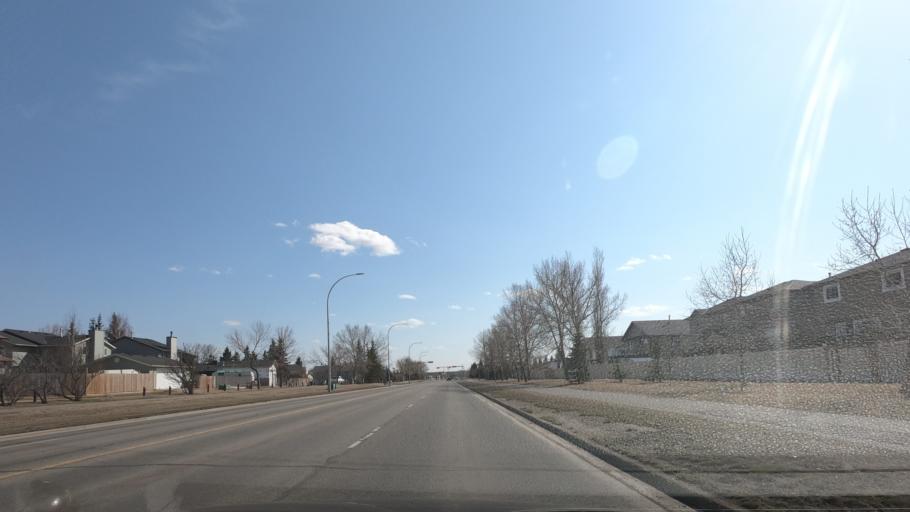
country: CA
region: Alberta
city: Airdrie
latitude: 51.2748
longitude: -113.9899
